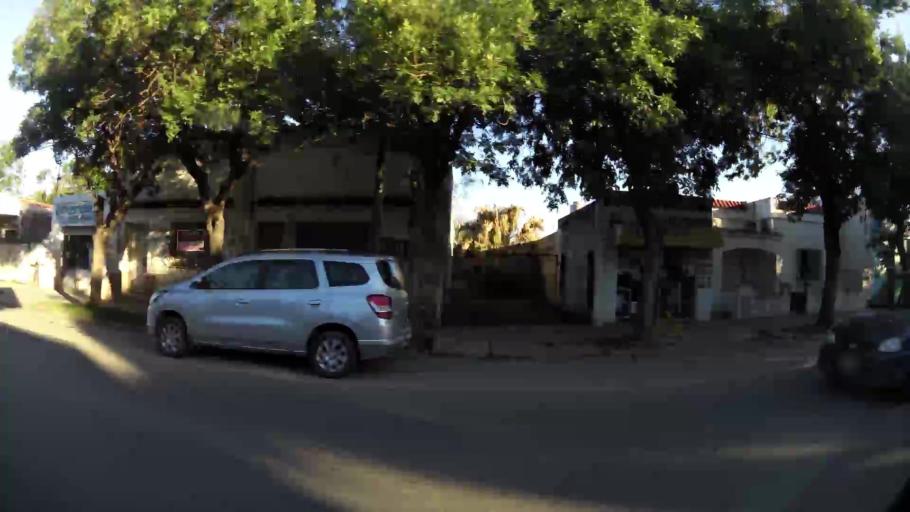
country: AR
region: Cordoba
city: Las Varillas
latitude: -31.8716
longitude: -62.7116
